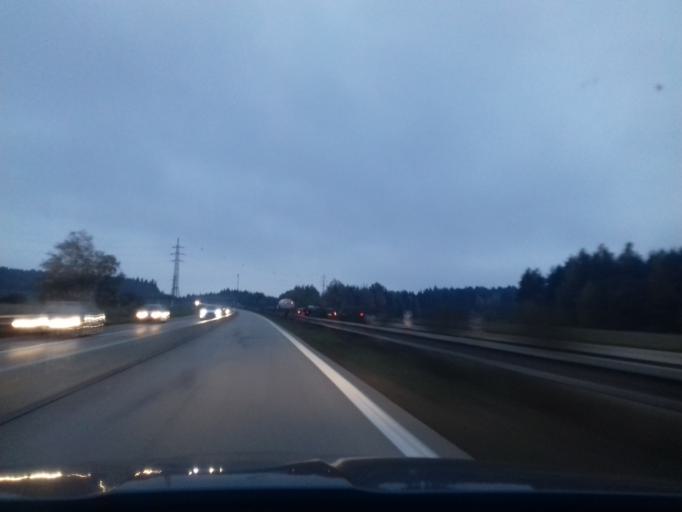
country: CZ
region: Vysocina
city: Velky Beranov
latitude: 49.4280
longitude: 15.6608
